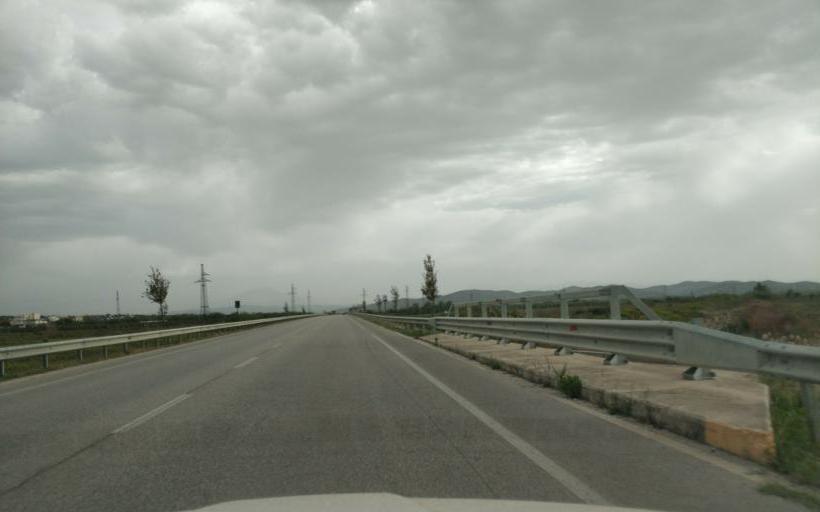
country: AL
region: Fier
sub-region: Rrethi i Fierit
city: Frakulla e Madhe
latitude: 40.6439
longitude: 19.4994
